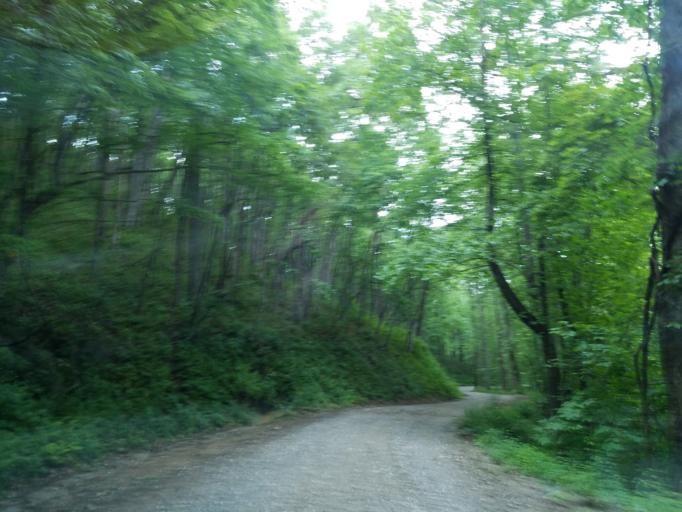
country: US
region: Georgia
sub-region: Lumpkin County
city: Dahlonega
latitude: 34.6607
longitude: -84.1311
